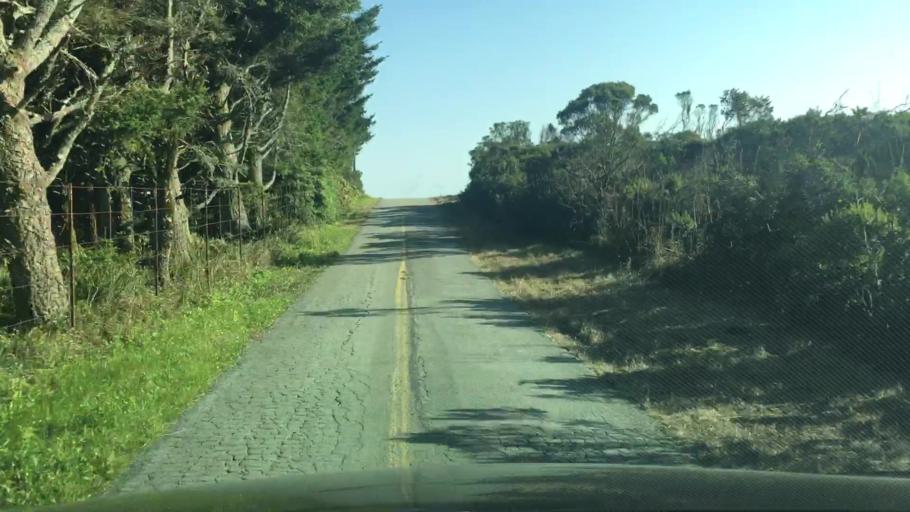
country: US
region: California
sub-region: San Mateo County
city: Highlands-Baywood Park
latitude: 37.5145
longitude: -122.3771
